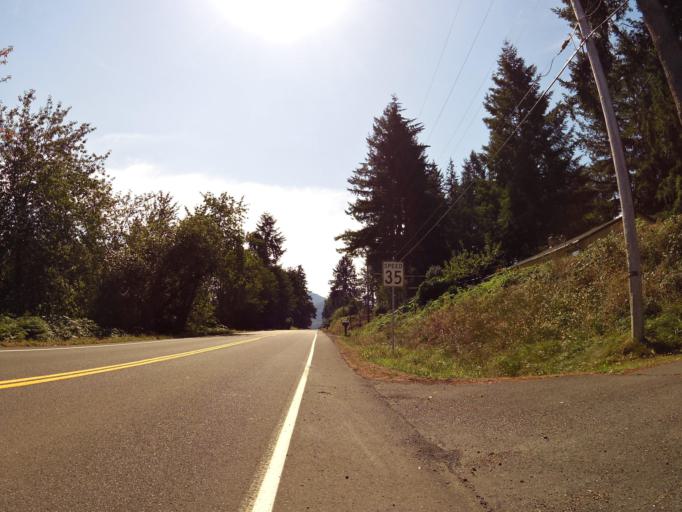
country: US
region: Washington
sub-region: Wahkiakum County
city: Cathlamet
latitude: 46.1774
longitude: -123.5832
